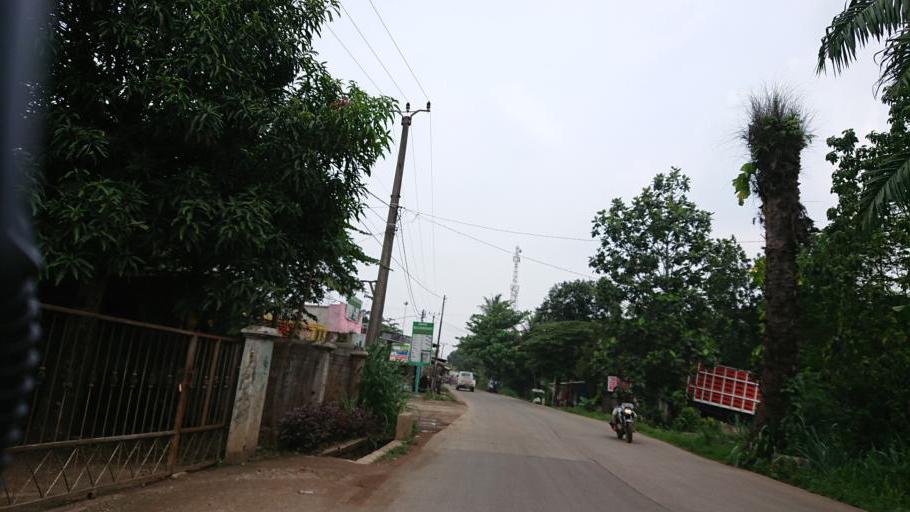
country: ID
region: West Java
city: Parung
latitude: -6.4593
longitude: 106.7058
